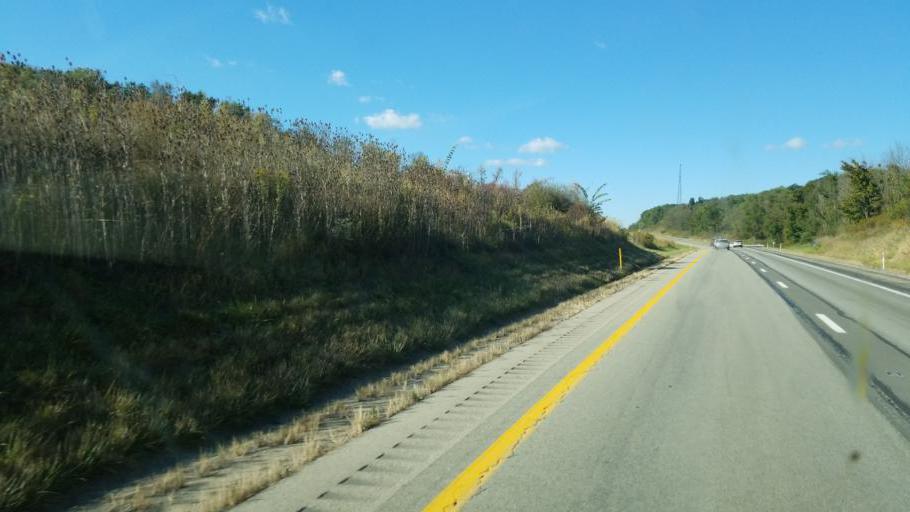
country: US
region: Pennsylvania
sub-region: Washington County
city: East Washington
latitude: 40.0634
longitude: -80.1870
